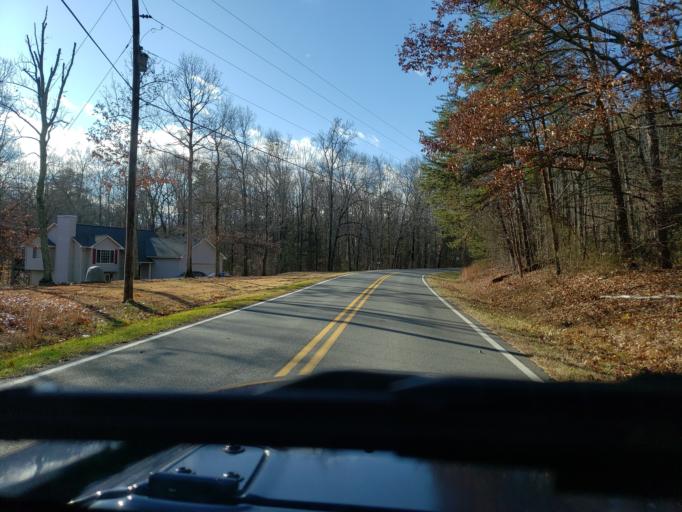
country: US
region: North Carolina
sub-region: Cleveland County
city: White Plains
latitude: 35.1708
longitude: -81.3598
